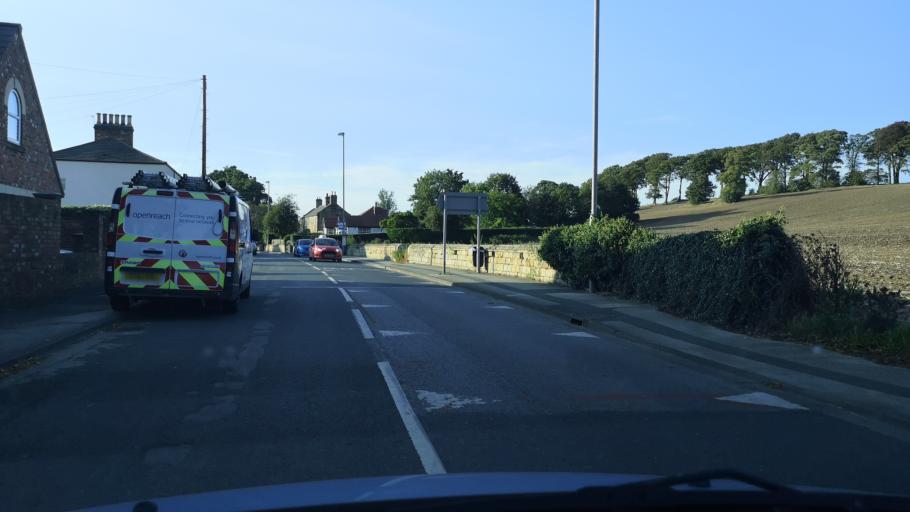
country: GB
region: England
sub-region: City and Borough of Wakefield
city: Pontefract
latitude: 53.6773
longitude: -1.2953
